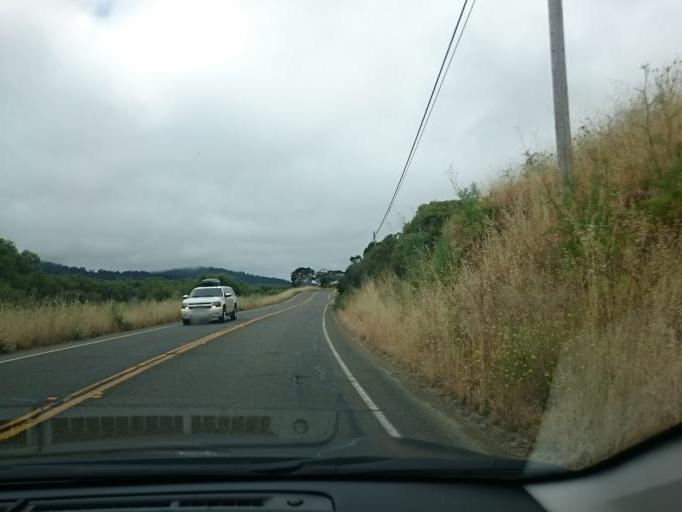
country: US
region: California
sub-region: Marin County
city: Inverness
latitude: 38.0536
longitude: -122.7964
